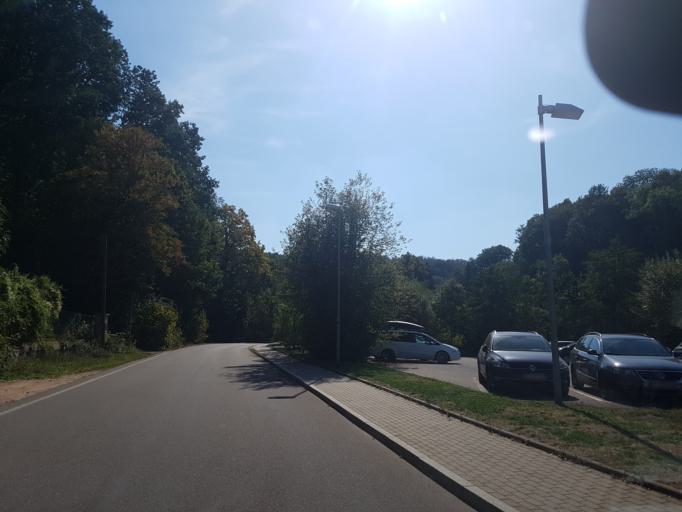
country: DE
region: Saxony
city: Kriebstein
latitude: 51.0454
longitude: 13.0183
